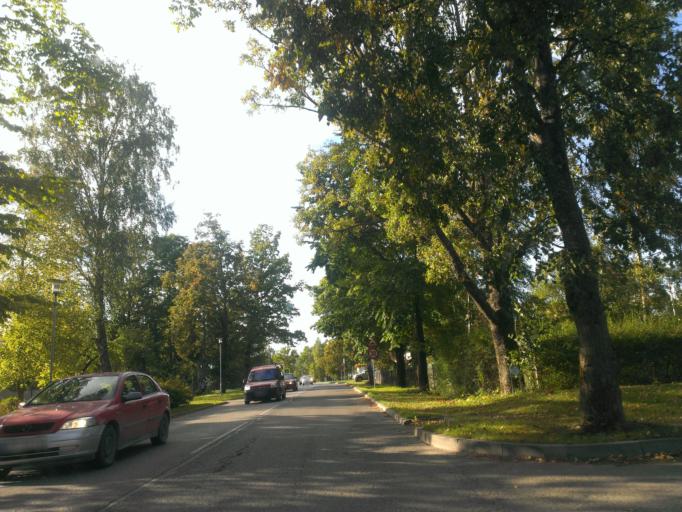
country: LV
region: Sigulda
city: Sigulda
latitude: 57.1602
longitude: 24.8624
